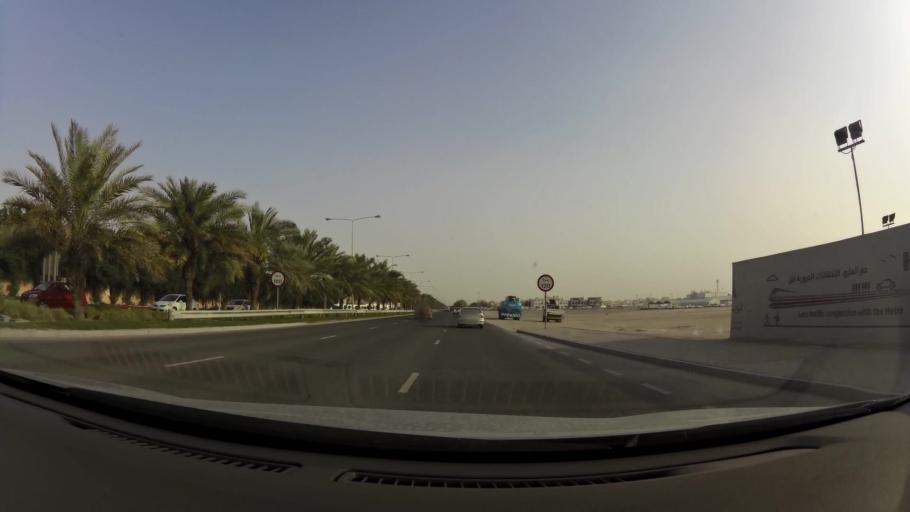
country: QA
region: Baladiyat ar Rayyan
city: Ar Rayyan
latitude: 25.2593
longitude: 51.4549
